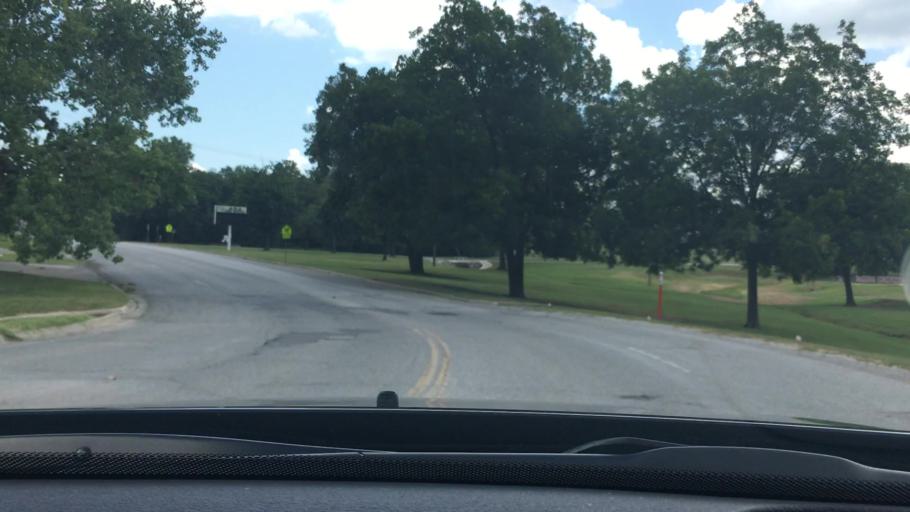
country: US
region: Oklahoma
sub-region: Pontotoc County
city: Ada
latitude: 34.7592
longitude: -96.6613
